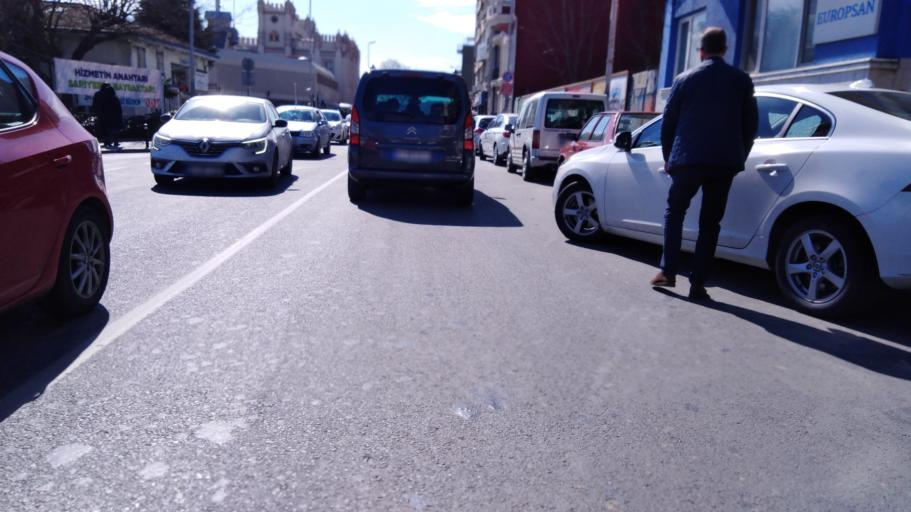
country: TR
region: Istanbul
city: Arikoey
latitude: 41.1669
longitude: 29.0571
